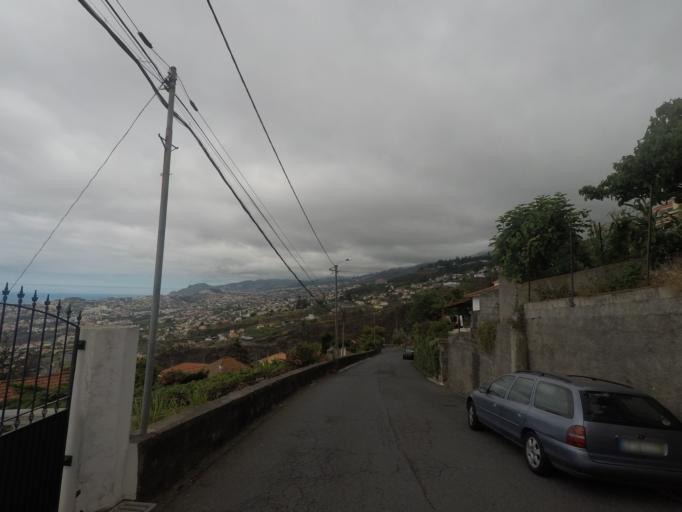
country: PT
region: Madeira
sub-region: Funchal
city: Nossa Senhora do Monte
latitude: 32.6652
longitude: -16.8931
